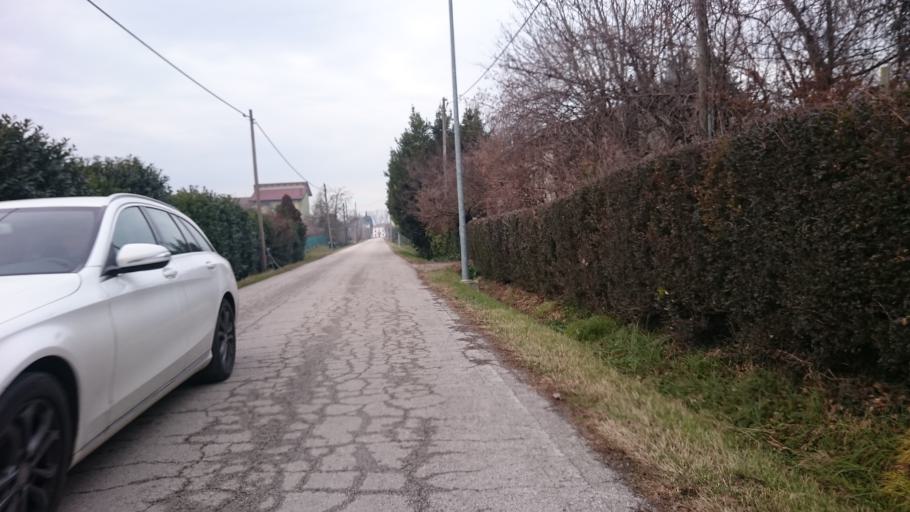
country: IT
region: Veneto
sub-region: Provincia di Vicenza
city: Grisignano di Zocco
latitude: 45.4895
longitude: 11.6964
